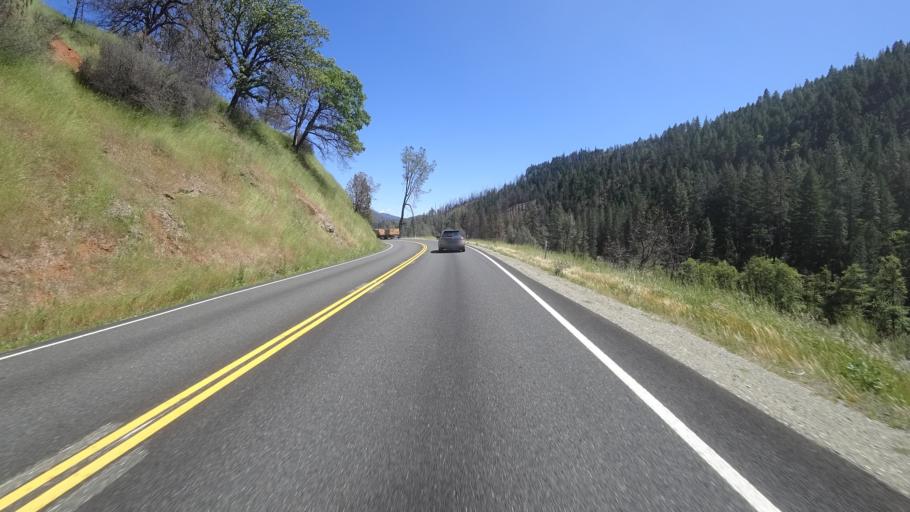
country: US
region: California
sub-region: Trinity County
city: Weaverville
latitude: 40.7668
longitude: -123.1171
